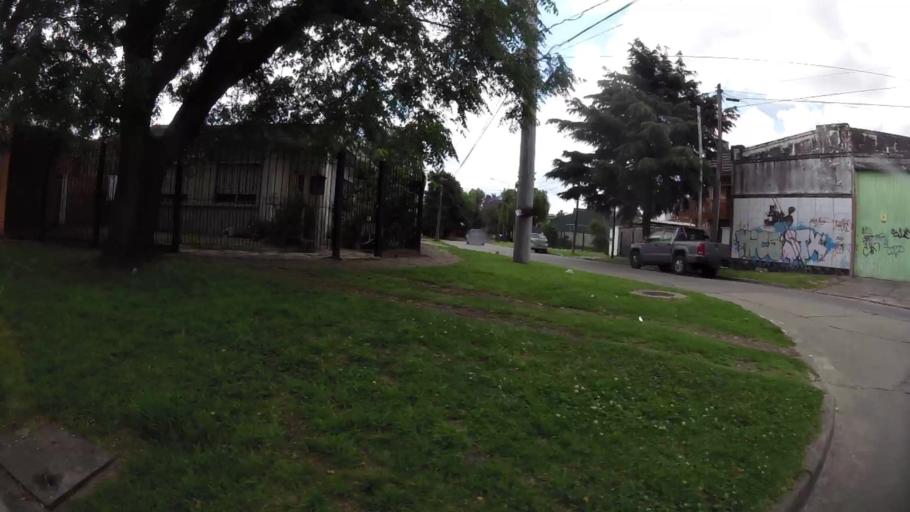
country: AR
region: Buenos Aires
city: Ituzaingo
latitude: -34.6355
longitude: -58.6552
